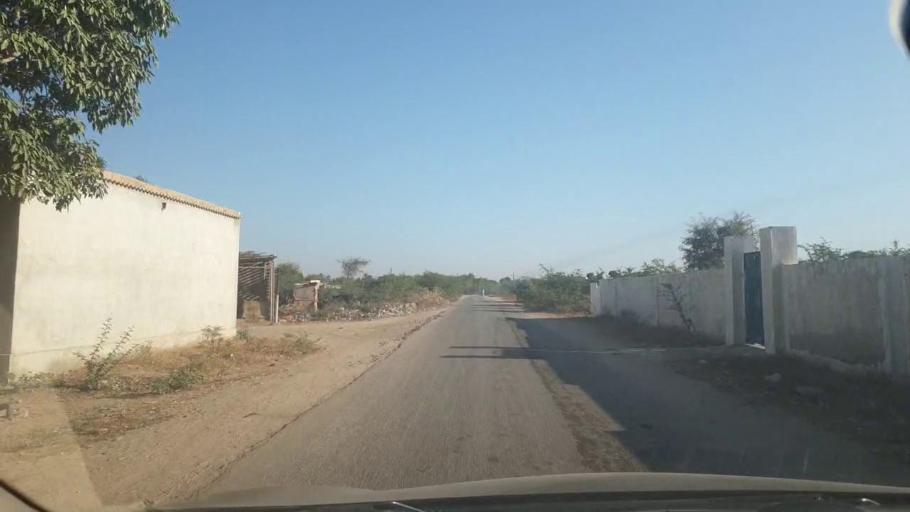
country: PK
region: Sindh
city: Malir Cantonment
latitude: 25.1013
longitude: 67.2563
